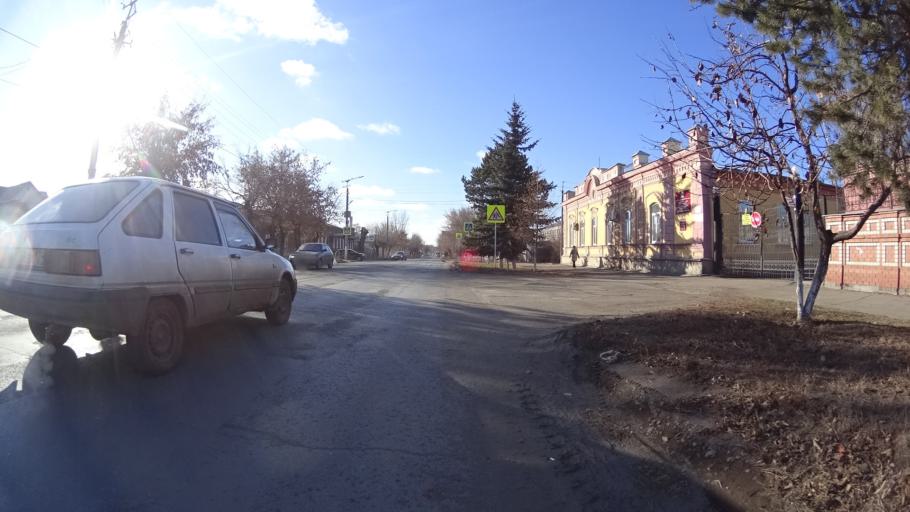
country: RU
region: Chelyabinsk
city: Troitsk
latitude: 54.0819
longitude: 61.5550
